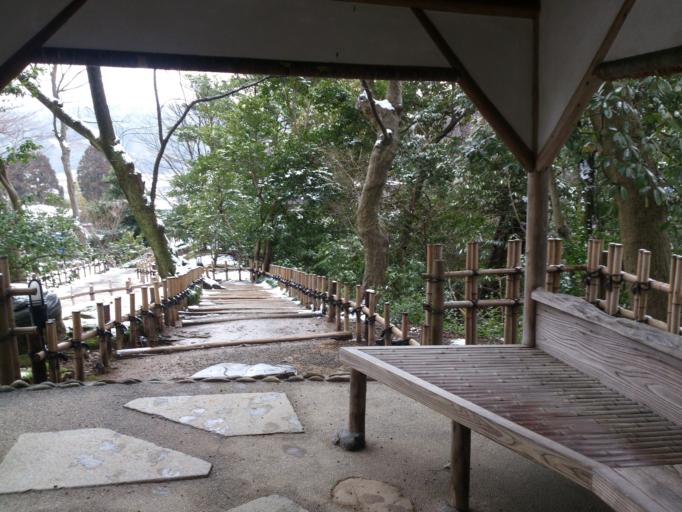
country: JP
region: Ishikawa
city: Kanazawa-shi
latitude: 36.5615
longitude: 136.6647
